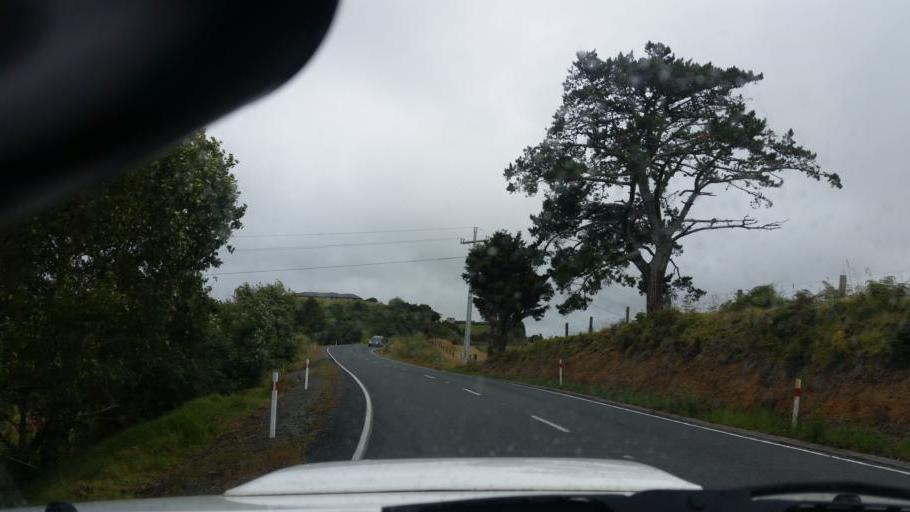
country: NZ
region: Auckland
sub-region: Auckland
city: Wellsford
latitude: -36.1353
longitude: 174.5268
